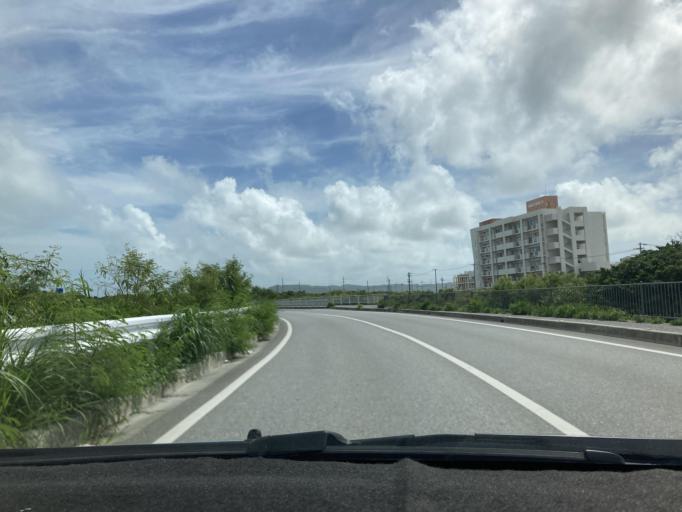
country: JP
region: Okinawa
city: Ginowan
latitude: 26.2115
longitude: 127.7622
